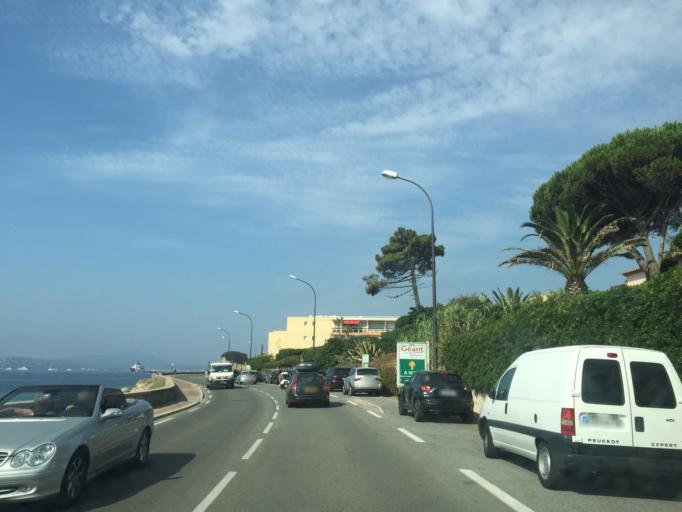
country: FR
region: Provence-Alpes-Cote d'Azur
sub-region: Departement du Var
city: Sainte-Maxime
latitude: 43.3078
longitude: 6.6475
